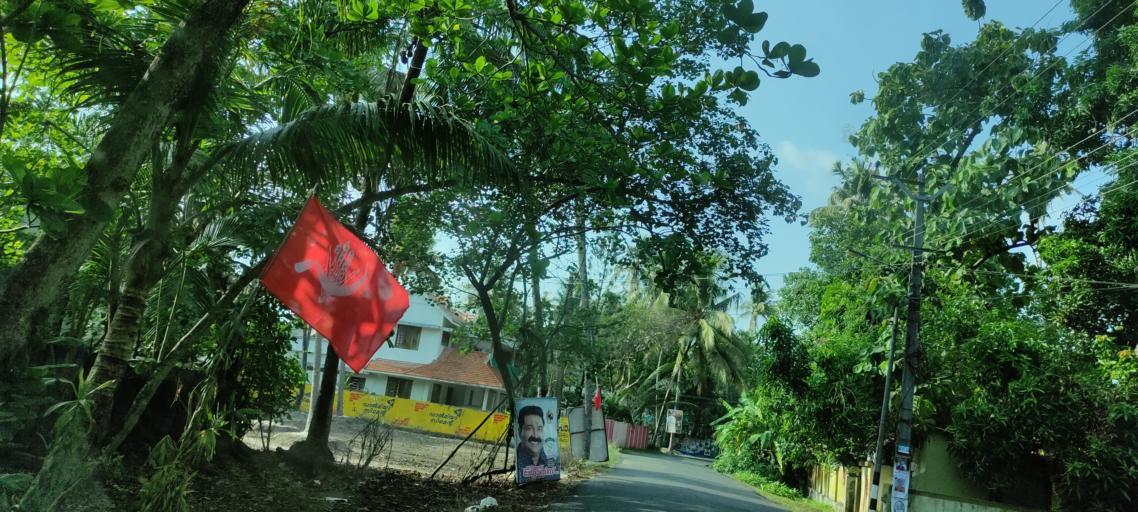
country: IN
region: Kerala
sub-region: Alappuzha
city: Vayalar
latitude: 9.7166
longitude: 76.2878
